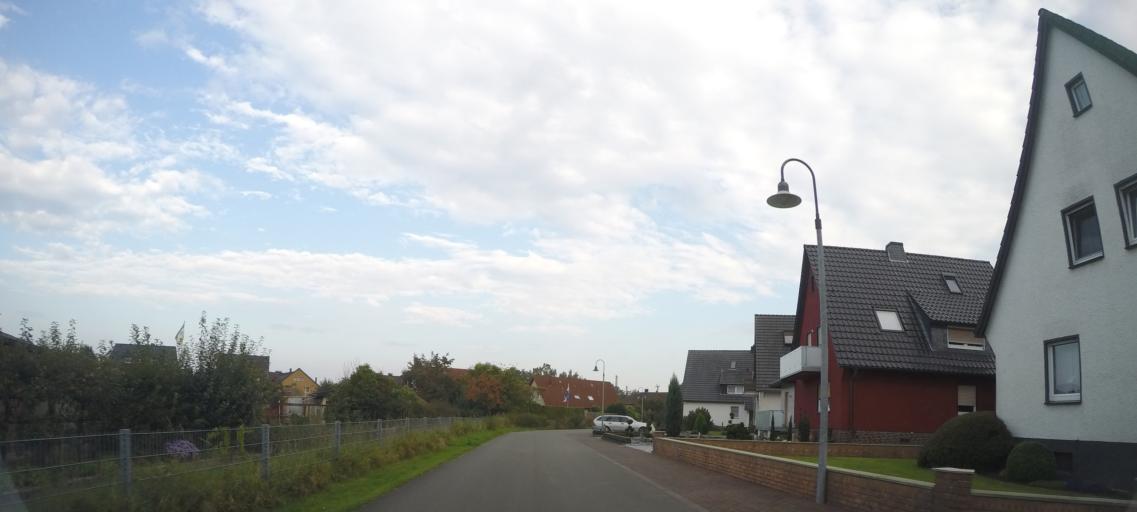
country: DE
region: North Rhine-Westphalia
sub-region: Regierungsbezirk Arnsberg
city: Lippstadt
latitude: 51.6693
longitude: 8.3291
